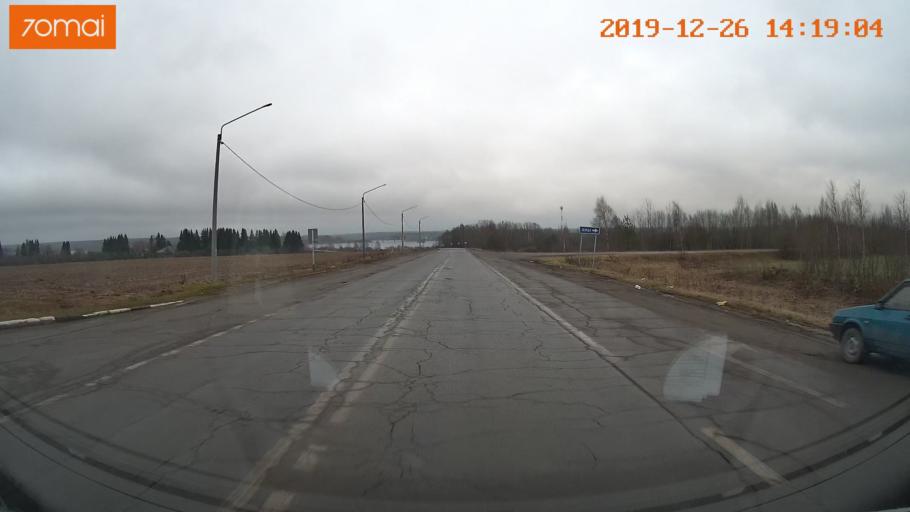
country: RU
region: Jaroslavl
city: Poshekhon'ye
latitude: 58.5119
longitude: 39.1083
